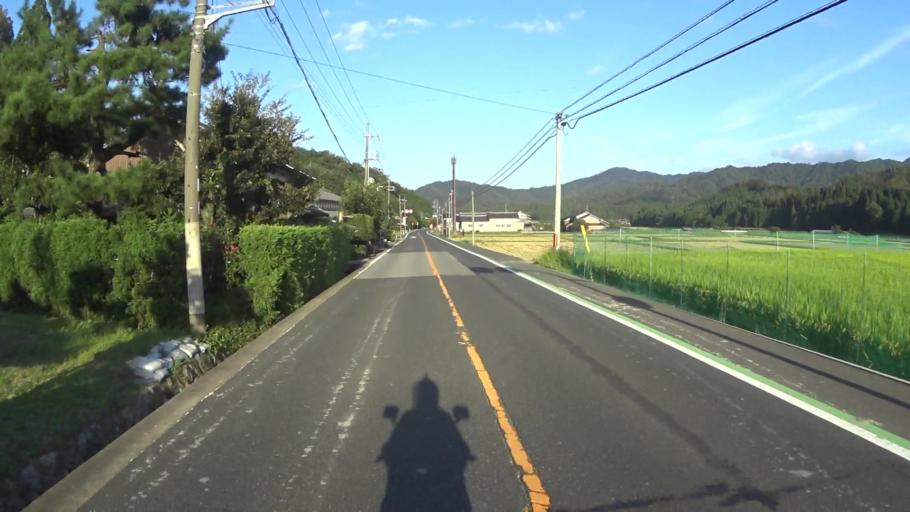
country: JP
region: Kyoto
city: Miyazu
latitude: 35.5802
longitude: 135.0241
